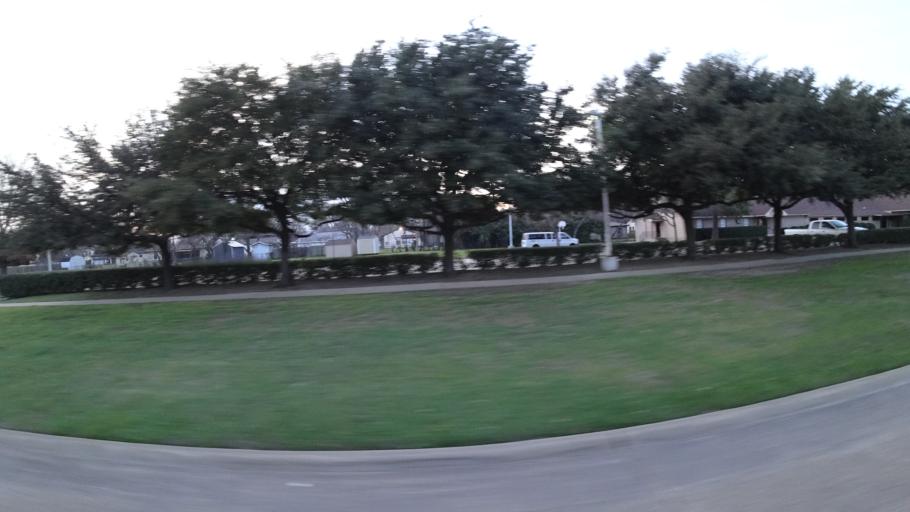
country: US
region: Texas
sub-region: Denton County
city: Lewisville
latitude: 33.0411
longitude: -96.9968
